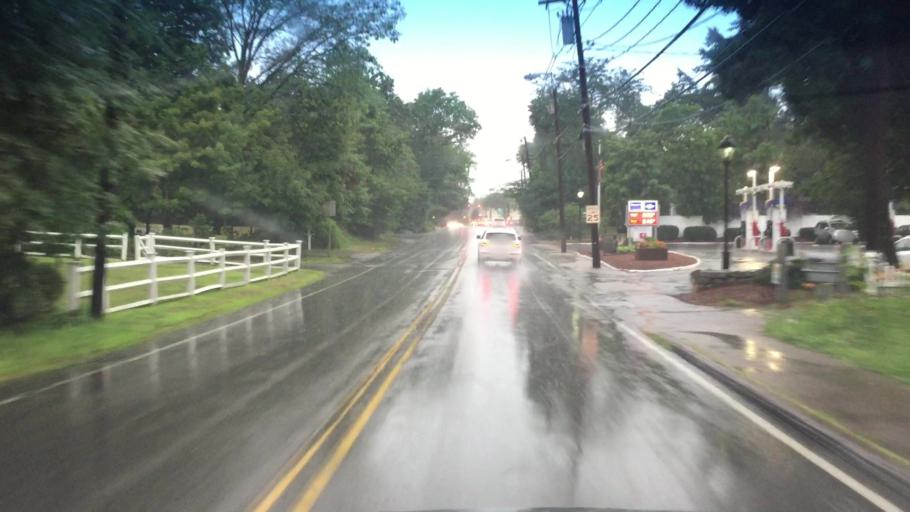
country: US
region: Massachusetts
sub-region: Norfolk County
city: Medfield
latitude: 42.1836
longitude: -71.3069
